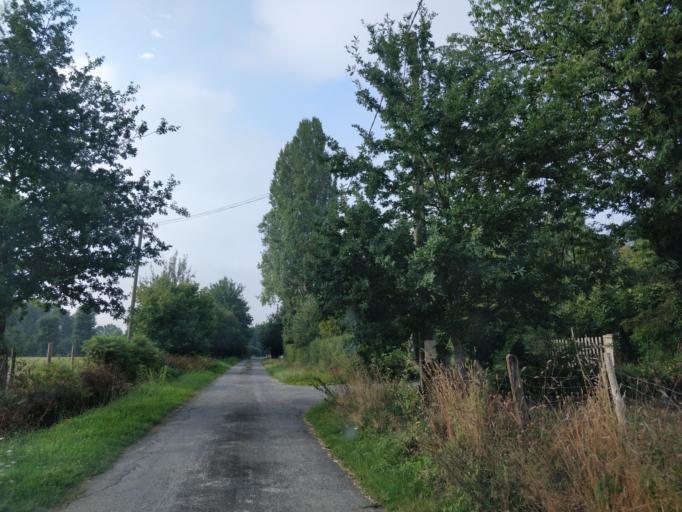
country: FR
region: Brittany
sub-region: Departement d'Ille-et-Vilaine
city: Noyal-sur-Vilaine
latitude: 48.1041
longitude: -1.5512
